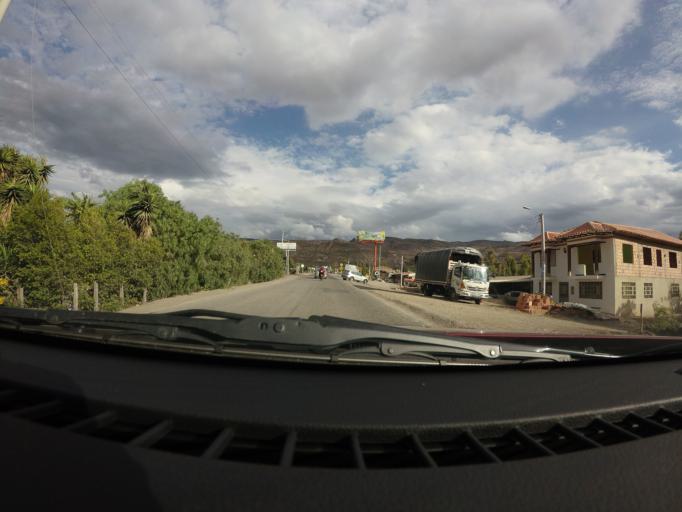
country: CO
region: Boyaca
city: Sachica
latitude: 5.5858
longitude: -73.5323
